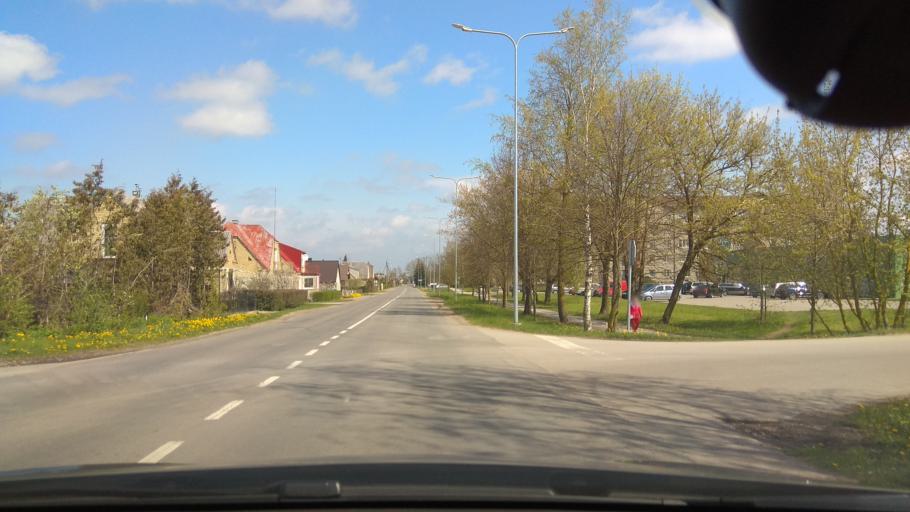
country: LT
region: Siauliu apskritis
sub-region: Joniskis
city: Joniskis
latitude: 56.2312
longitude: 23.6106
